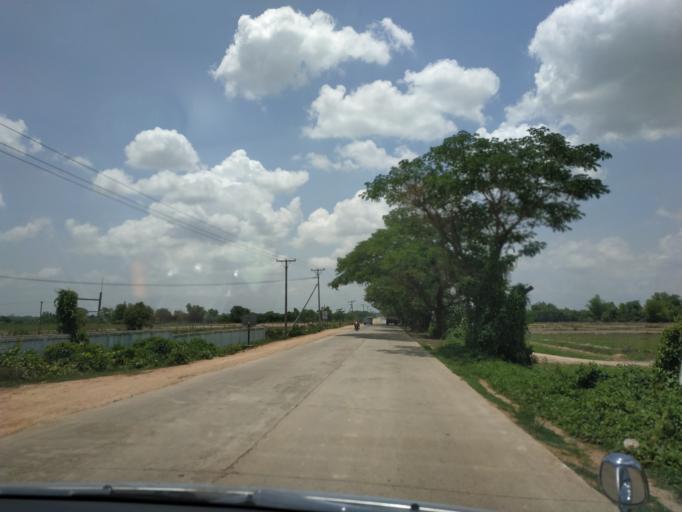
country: MM
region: Bago
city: Bago
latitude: 17.4795
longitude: 96.4894
